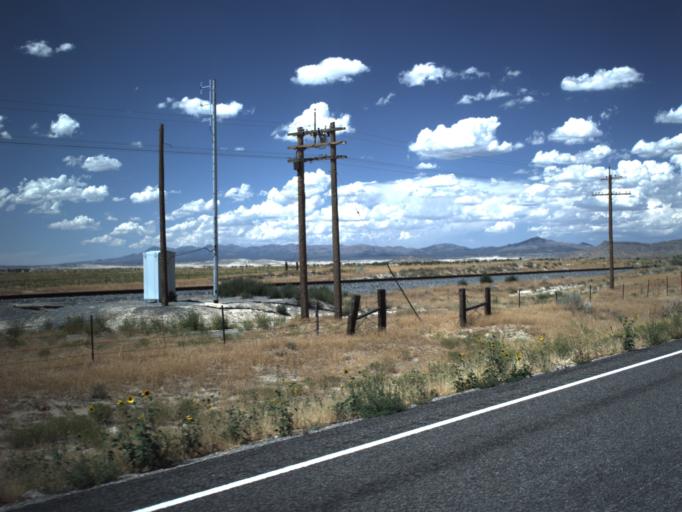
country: US
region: Utah
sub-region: Millard County
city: Delta
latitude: 39.5858
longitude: -112.3334
